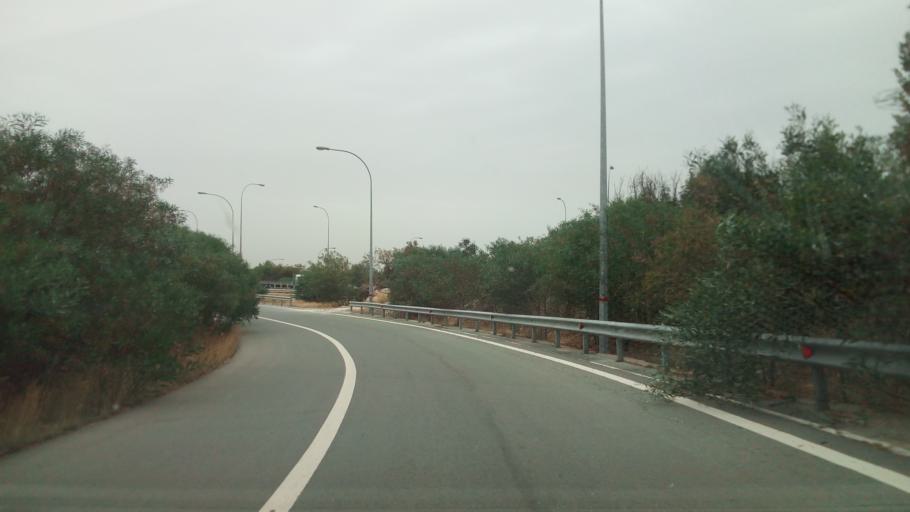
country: CY
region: Larnaka
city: Kofinou
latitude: 34.8394
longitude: 33.3973
